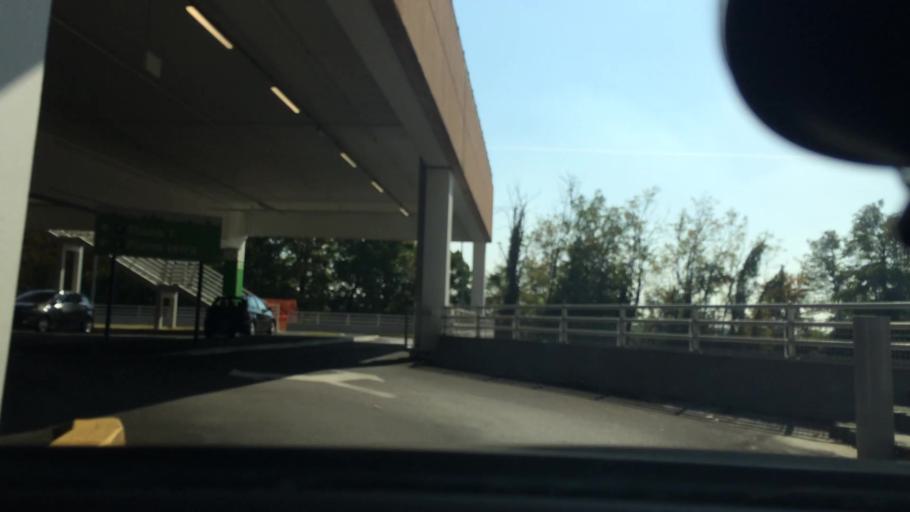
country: IT
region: Lombardy
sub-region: Citta metropolitana di Milano
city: Cerro Maggiore
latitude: 45.6092
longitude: 8.9645
